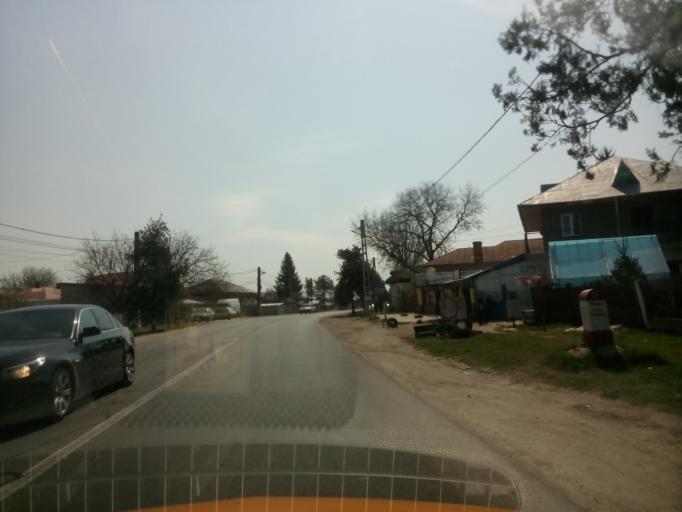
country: RO
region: Calarasi
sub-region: Comuna Frumusani
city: Frumusani
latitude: 44.3022
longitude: 26.3050
